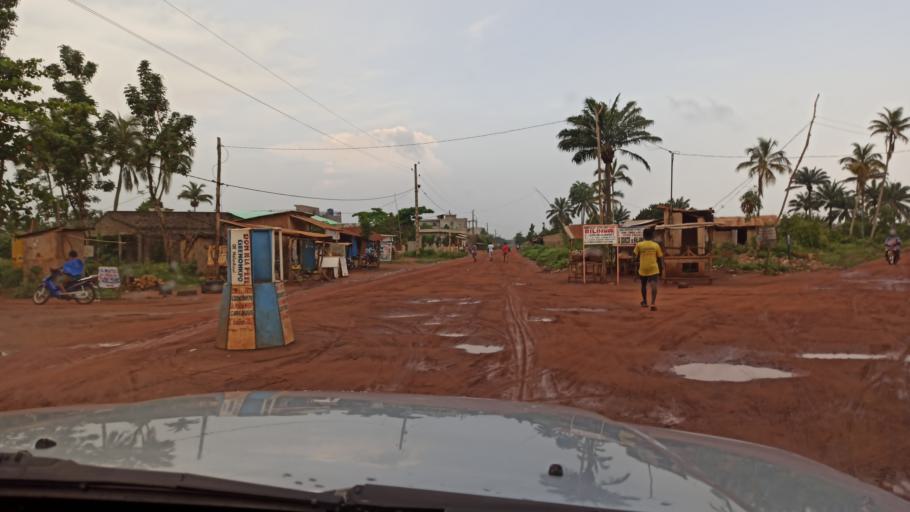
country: BJ
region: Queme
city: Porto-Novo
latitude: 6.4904
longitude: 2.6689
